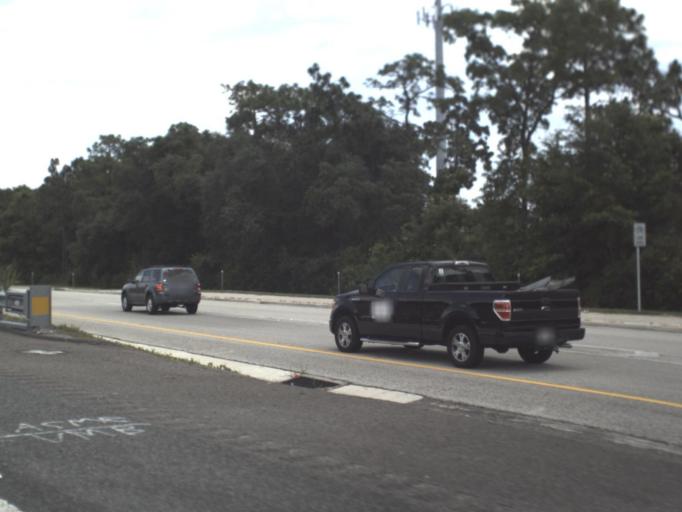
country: US
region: Florida
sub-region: Duval County
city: Jacksonville
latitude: 30.3501
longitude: -81.5523
